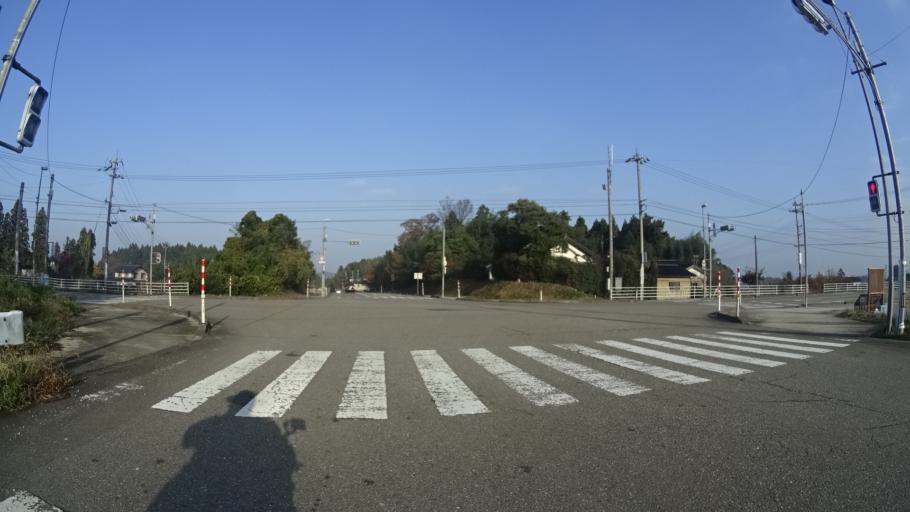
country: JP
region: Ishikawa
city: Nanao
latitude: 37.0256
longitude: 136.9766
